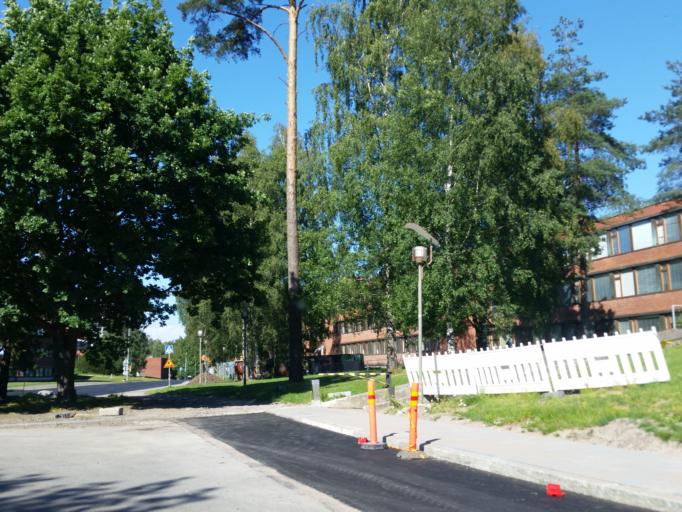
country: FI
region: Uusimaa
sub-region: Helsinki
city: Otaniemi
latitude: 60.1863
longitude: 24.8271
